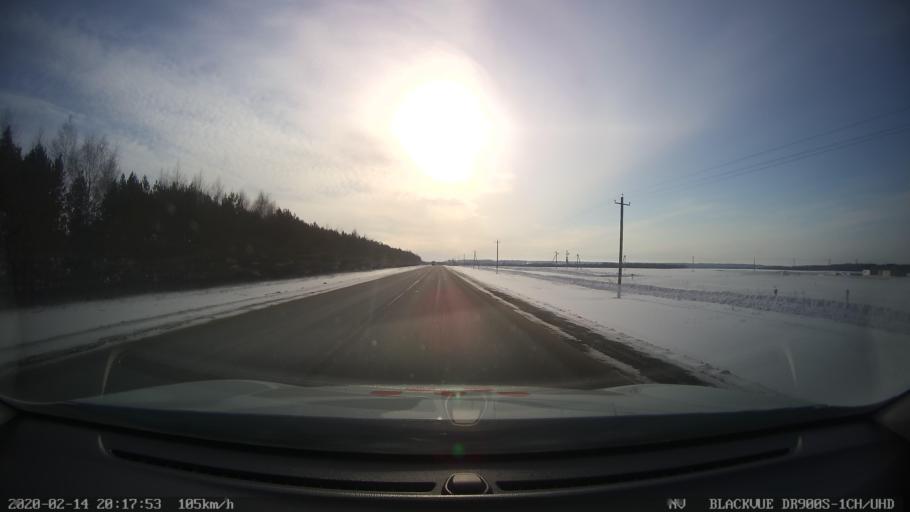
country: RU
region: Tatarstan
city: Verkhniy Uslon
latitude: 55.5940
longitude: 48.8817
